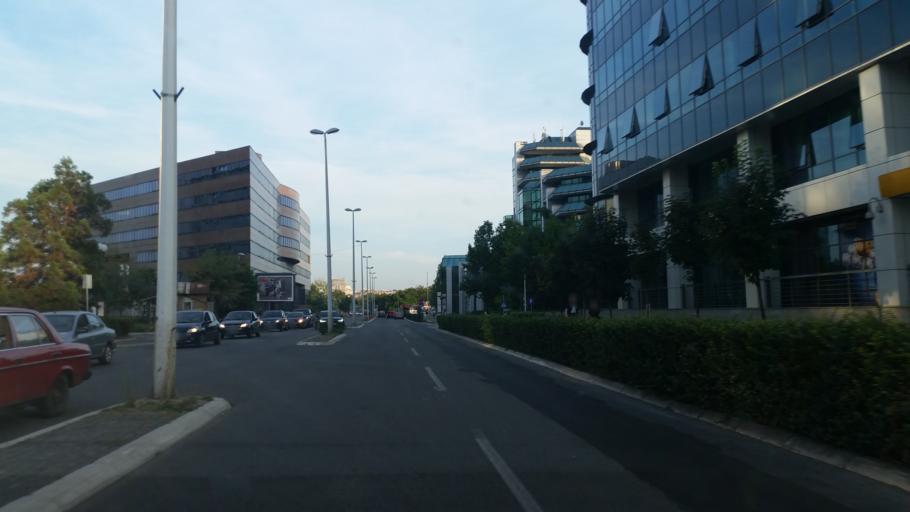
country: RS
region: Central Serbia
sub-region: Belgrade
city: Novi Beograd
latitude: 44.8120
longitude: 20.4352
